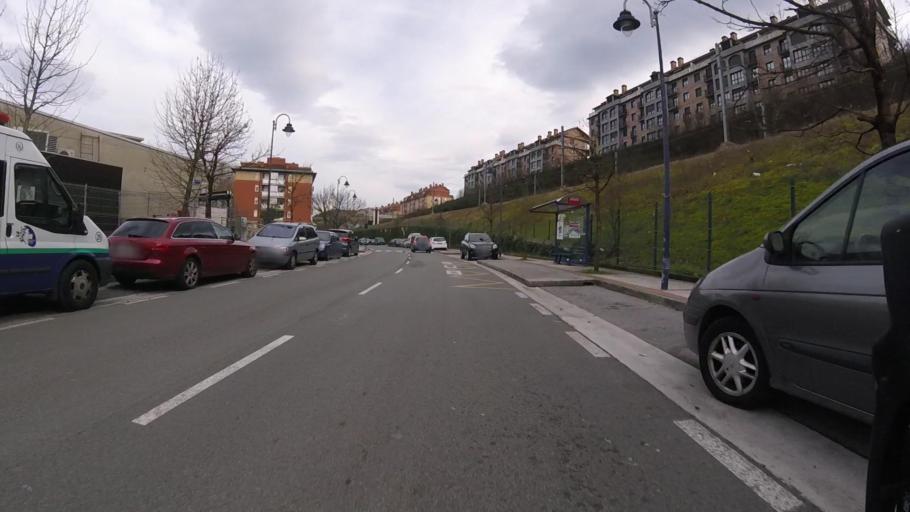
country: ES
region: Basque Country
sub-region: Provincia de Guipuzcoa
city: Errenteria
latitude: 43.3085
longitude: -1.8916
